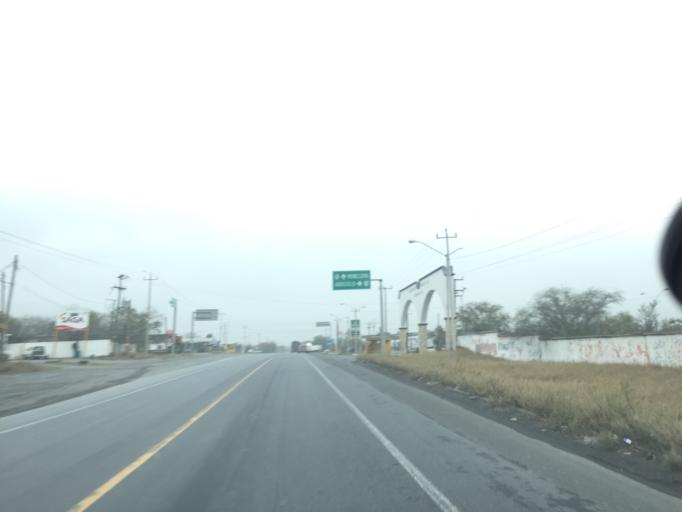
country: MX
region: Nuevo Leon
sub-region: Salinas Victoria
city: Las Torres
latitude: 25.9393
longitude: -100.4034
